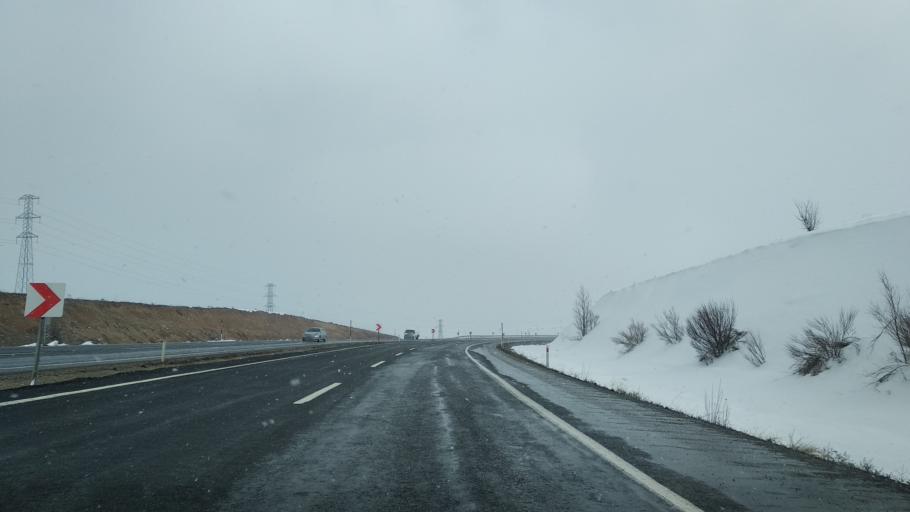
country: TR
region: Kayseri
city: Gesi
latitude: 38.6306
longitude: 35.7374
